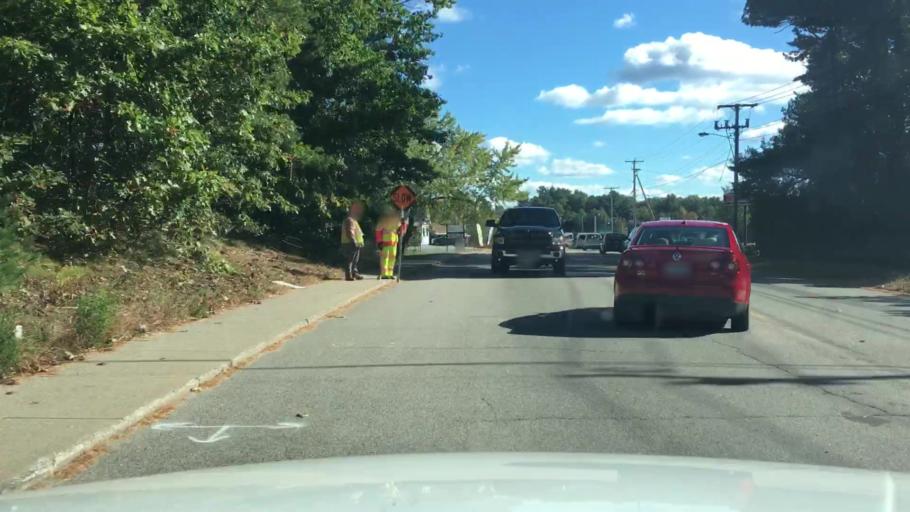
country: US
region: Maine
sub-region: York County
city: South Sanford
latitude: 43.4227
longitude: -70.7589
